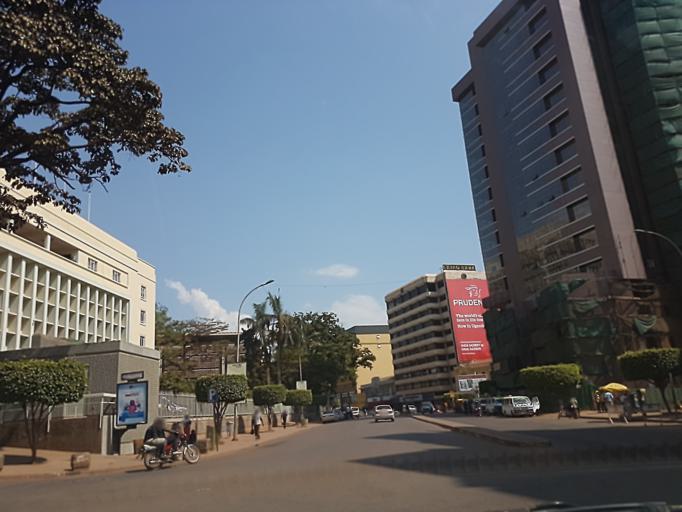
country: UG
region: Central Region
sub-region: Kampala District
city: Kampala
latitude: 0.3141
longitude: 32.5790
